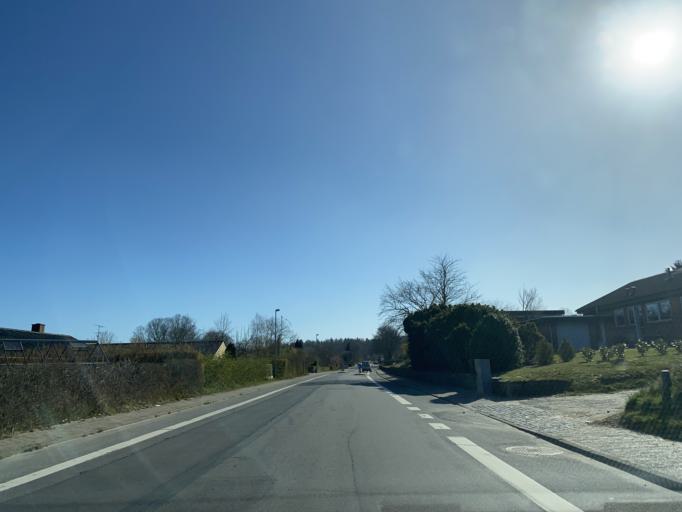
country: DK
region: Central Jutland
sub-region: Favrskov Kommune
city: Ulstrup
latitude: 56.3867
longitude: 9.7808
